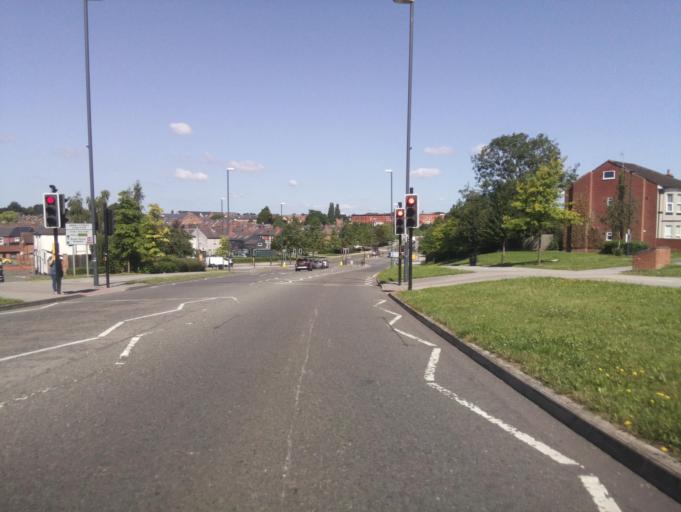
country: GB
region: England
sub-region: Derby
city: Derby
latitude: 52.9190
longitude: -1.4818
